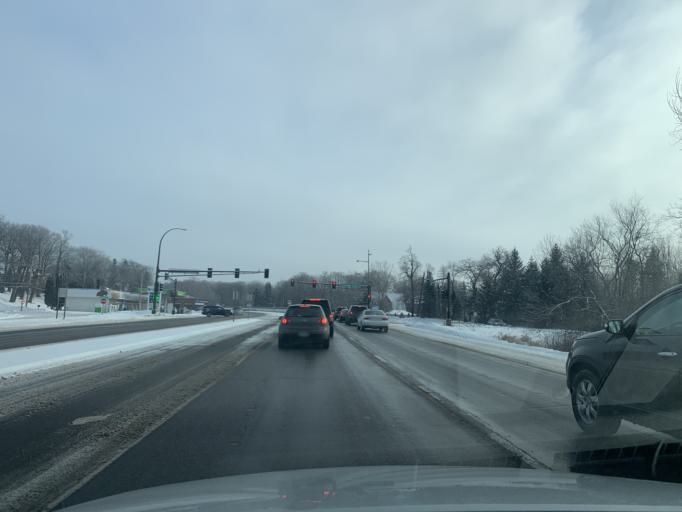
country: US
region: Minnesota
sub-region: Hennepin County
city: Excelsior
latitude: 44.9019
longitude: -93.5520
